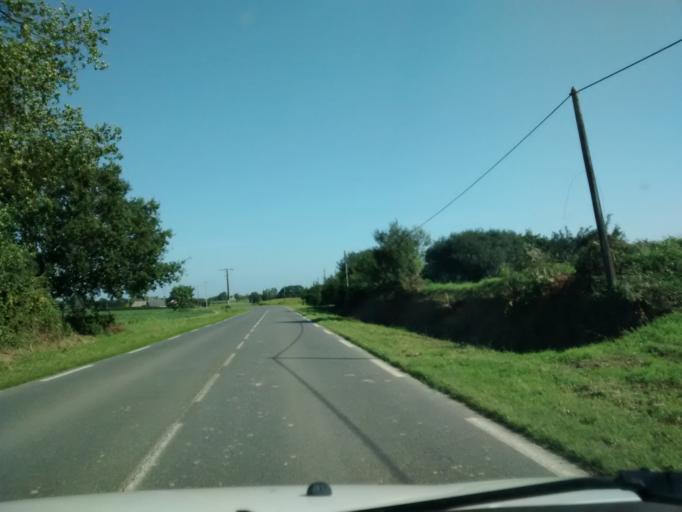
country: FR
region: Brittany
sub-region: Departement des Cotes-d'Armor
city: Tredarzec
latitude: 48.8196
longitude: -3.1896
